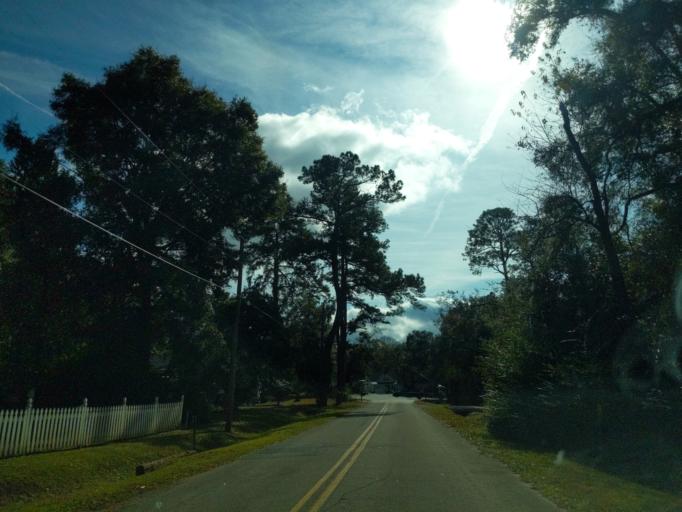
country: US
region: Florida
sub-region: Leon County
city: Tallahassee
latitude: 30.4706
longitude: -84.2019
